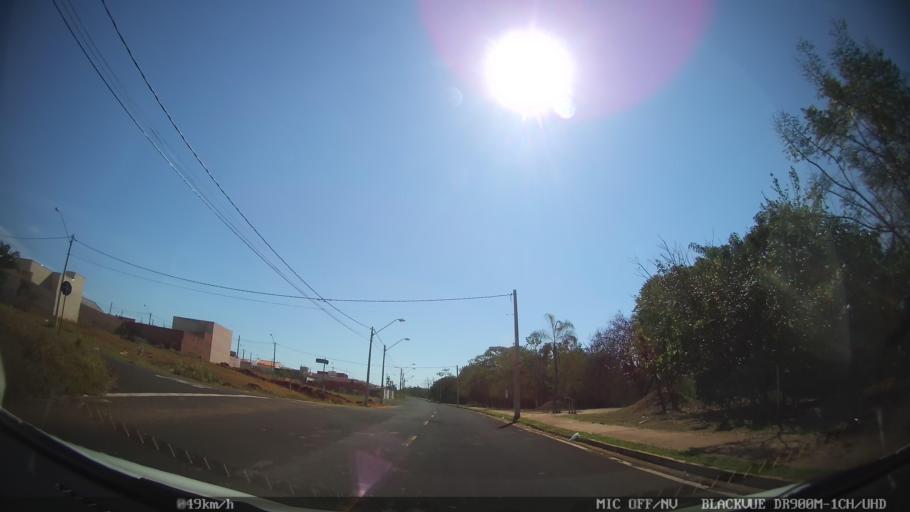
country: BR
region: Sao Paulo
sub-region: Sao Jose Do Rio Preto
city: Sao Jose do Rio Preto
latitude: -20.7591
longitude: -49.4204
